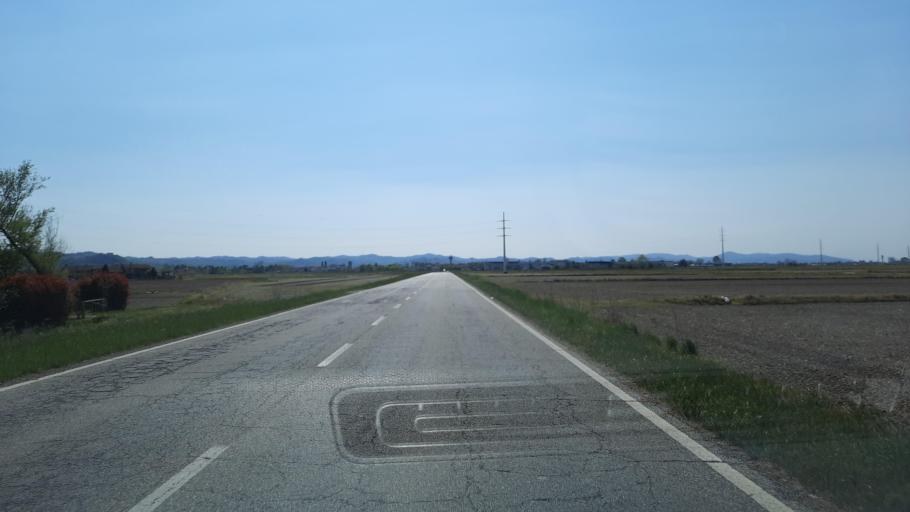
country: IT
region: Piedmont
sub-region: Provincia di Vercelli
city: Lamporo
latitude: 45.2061
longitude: 8.1187
